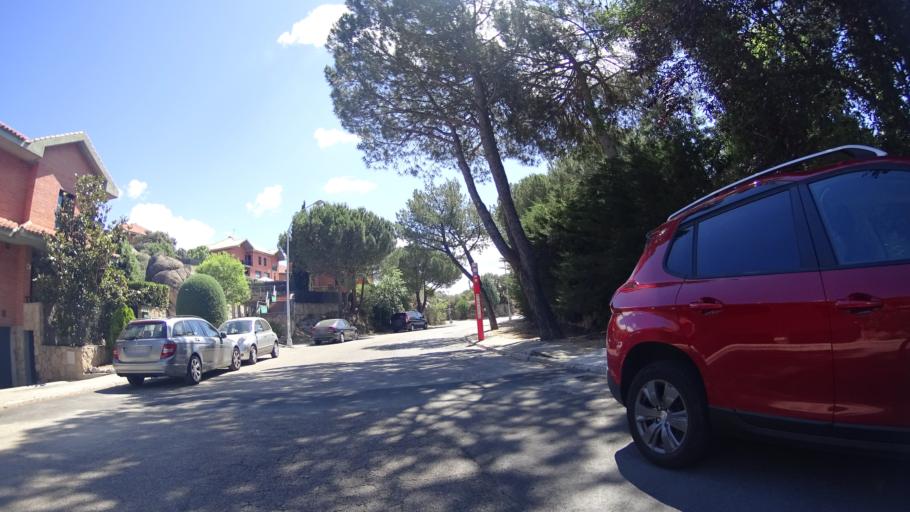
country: ES
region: Madrid
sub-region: Provincia de Madrid
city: Torrelodones
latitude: 40.5855
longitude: -3.9211
